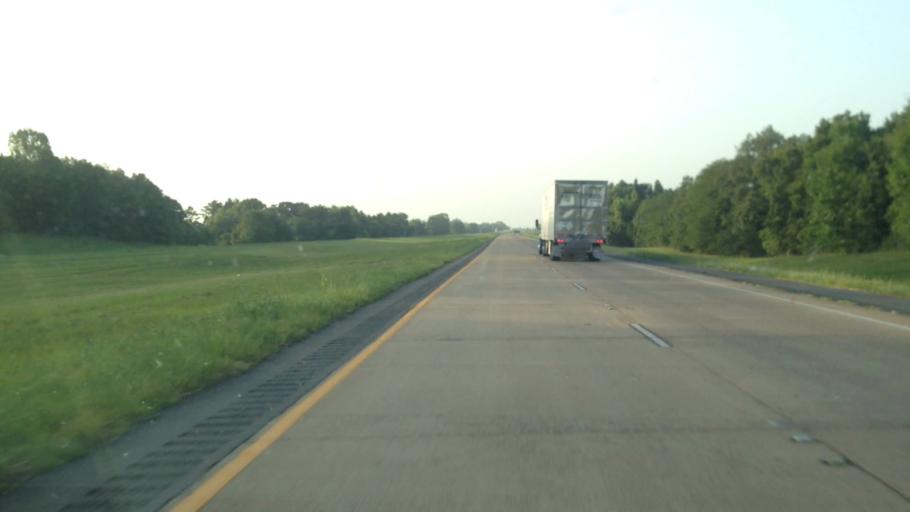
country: US
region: Louisiana
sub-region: Natchitoches Parish
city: Vienna Bend
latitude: 31.6353
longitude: -93.0746
